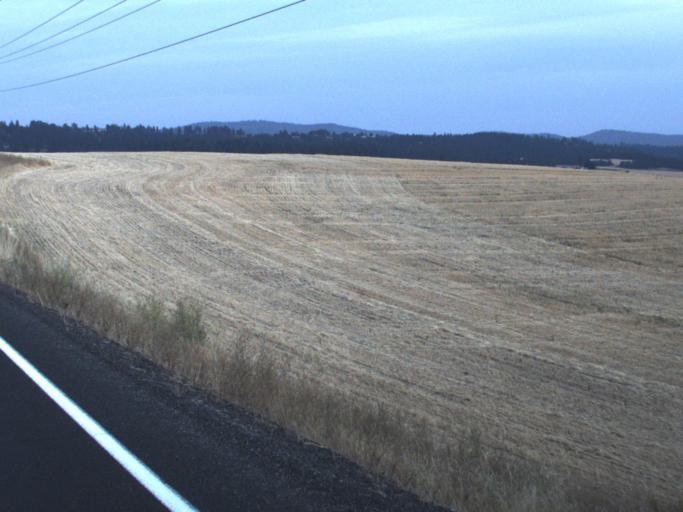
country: US
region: Washington
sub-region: Spokane County
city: Mead
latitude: 47.7875
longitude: -117.2750
